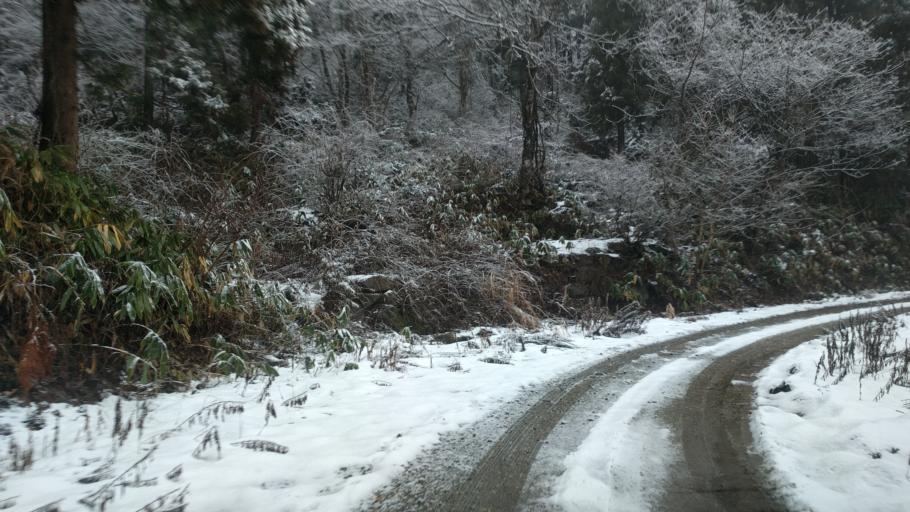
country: JP
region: Fukushima
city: Inawashiro
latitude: 37.5771
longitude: 139.9900
